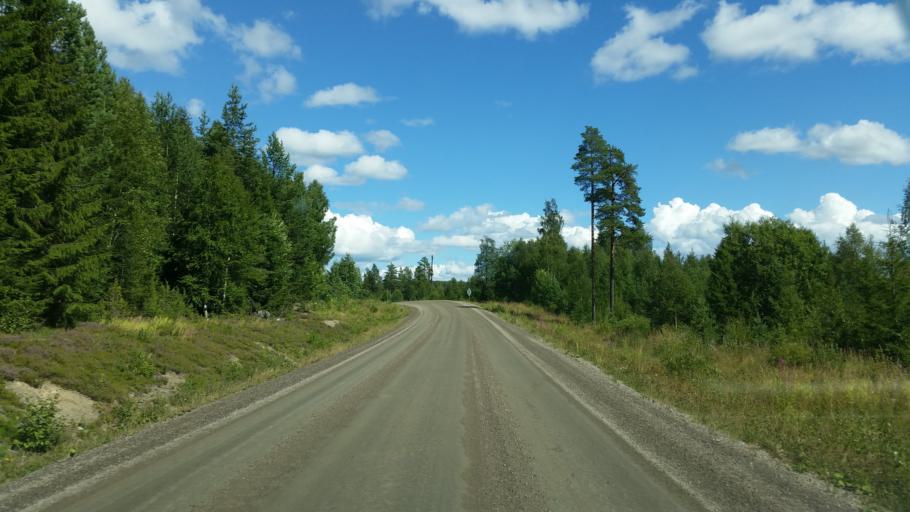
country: SE
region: Gaevleborg
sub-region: Ljusdals Kommun
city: Ljusdal
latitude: 61.9254
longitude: 16.1536
